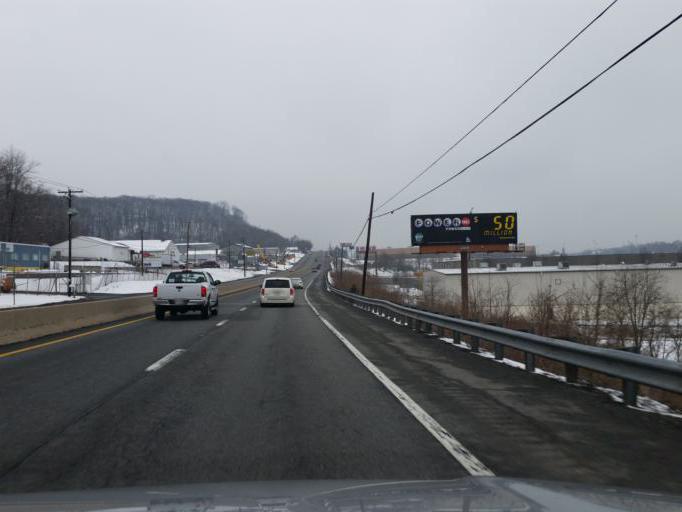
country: US
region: Pennsylvania
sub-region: Dauphin County
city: Rutherford
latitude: 40.2615
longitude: -76.7612
